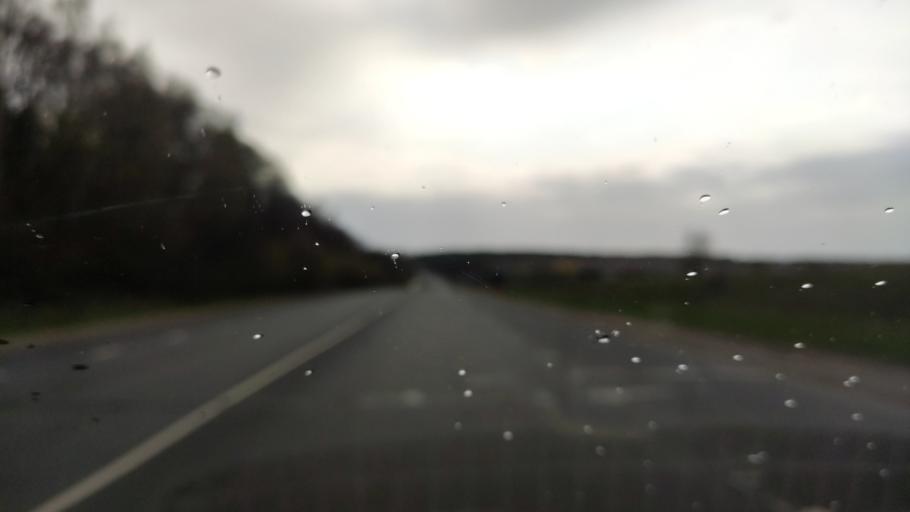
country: RU
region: Kursk
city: Gorshechnoye
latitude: 51.4721
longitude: 37.9413
